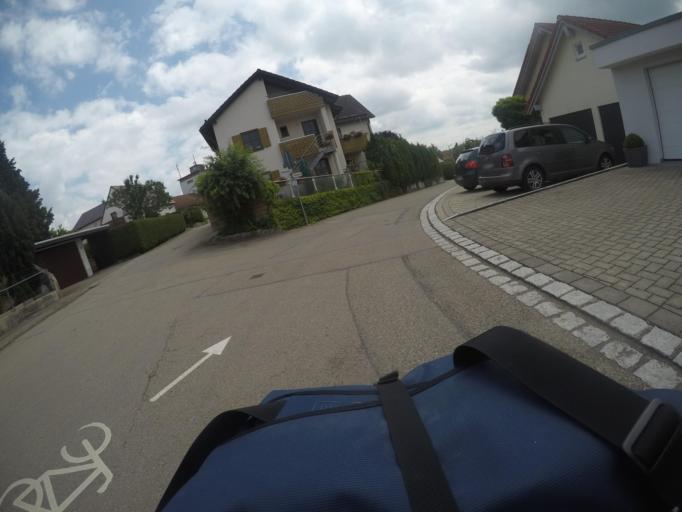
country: DE
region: Bavaria
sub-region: Swabia
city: Heimertingen
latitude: 48.0368
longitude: 10.1595
